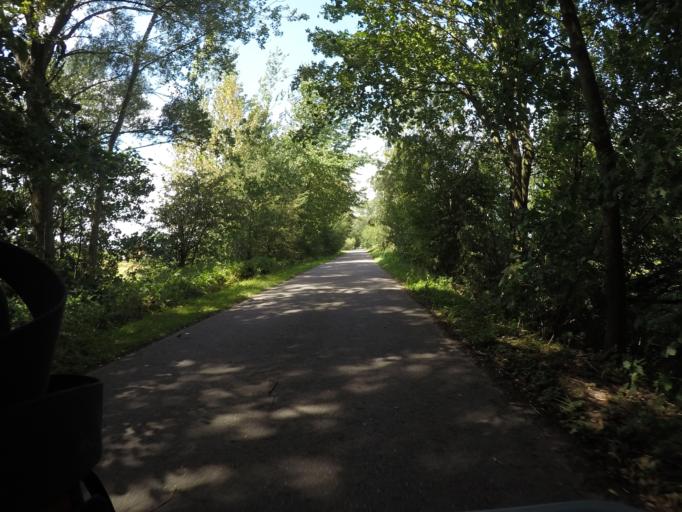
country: DE
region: Lower Saxony
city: Stelle
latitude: 53.4302
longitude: 10.1490
